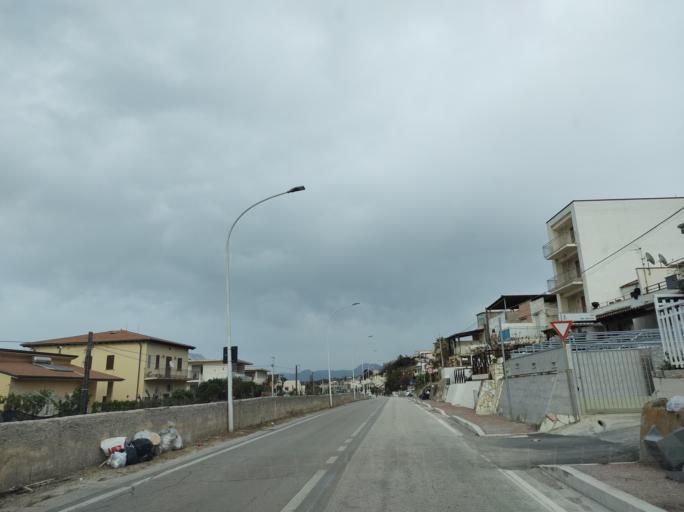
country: IT
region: Sicily
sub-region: Trapani
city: Alcamo
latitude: 38.0301
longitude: 12.9462
